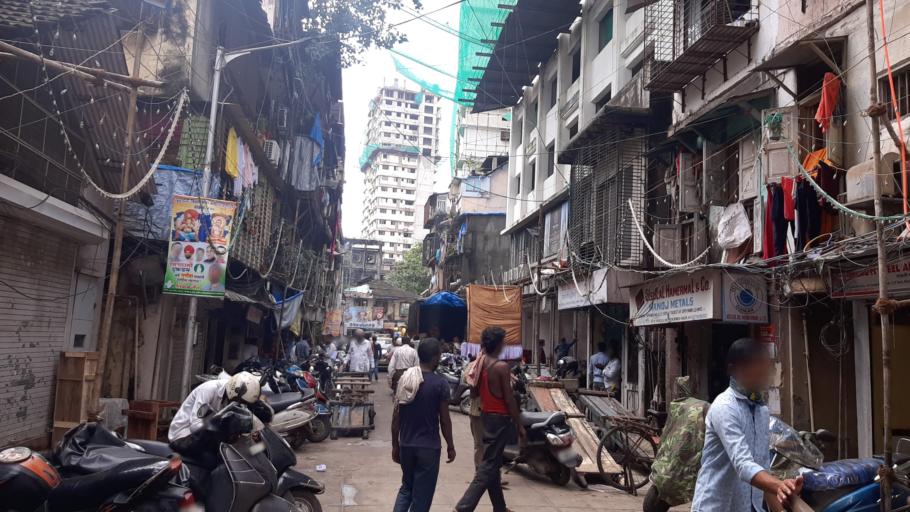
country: IN
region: Maharashtra
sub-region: Mumbai Suburban
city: Mumbai
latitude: 18.9563
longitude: 72.8272
